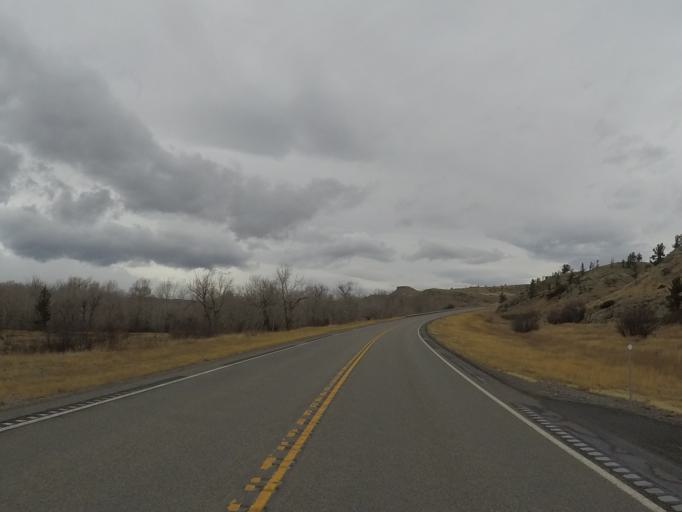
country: US
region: Montana
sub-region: Sweet Grass County
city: Big Timber
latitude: 45.9300
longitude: -109.9855
